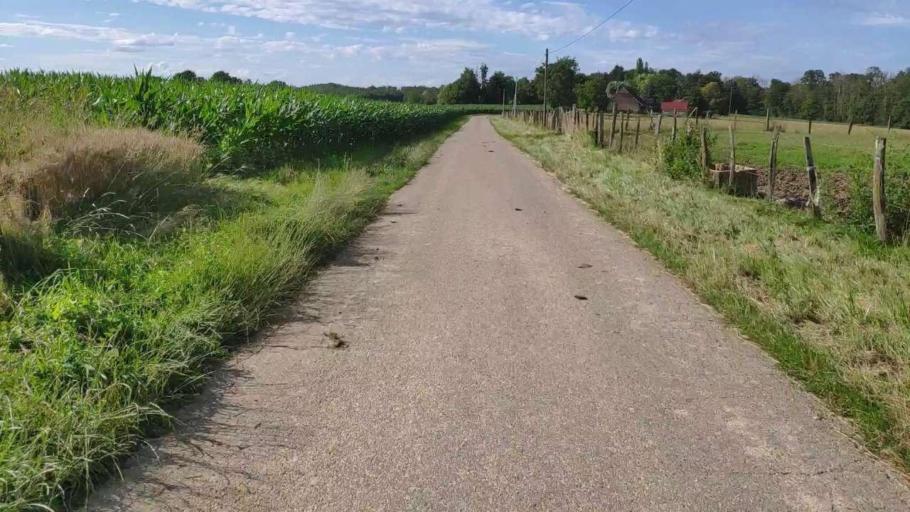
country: FR
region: Franche-Comte
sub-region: Departement du Jura
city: Bletterans
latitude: 46.8106
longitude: 5.4962
